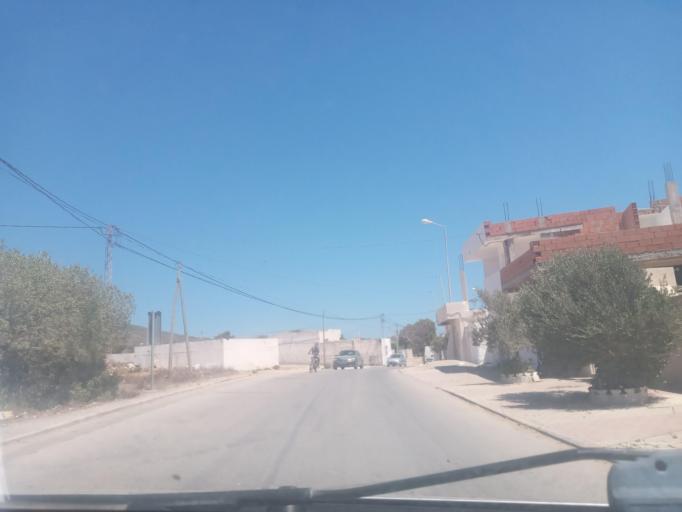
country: TN
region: Nabul
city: El Haouaria
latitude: 37.0558
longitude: 11.0019
